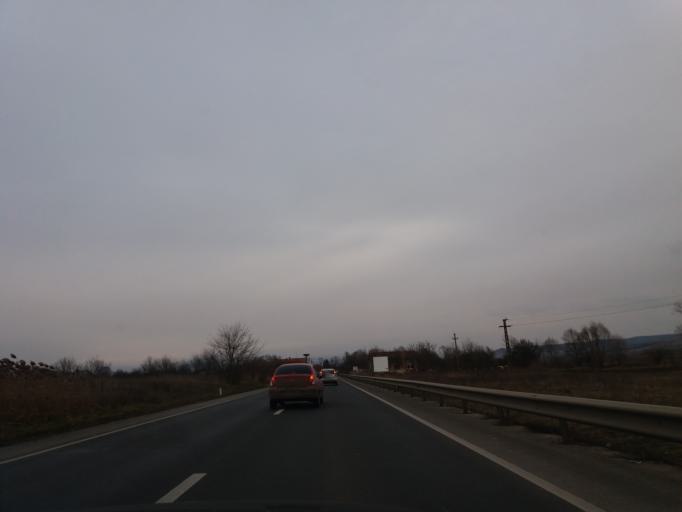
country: RO
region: Hunedoara
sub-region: Comuna Bacia
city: Bacia
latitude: 45.7704
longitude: 23.0010
